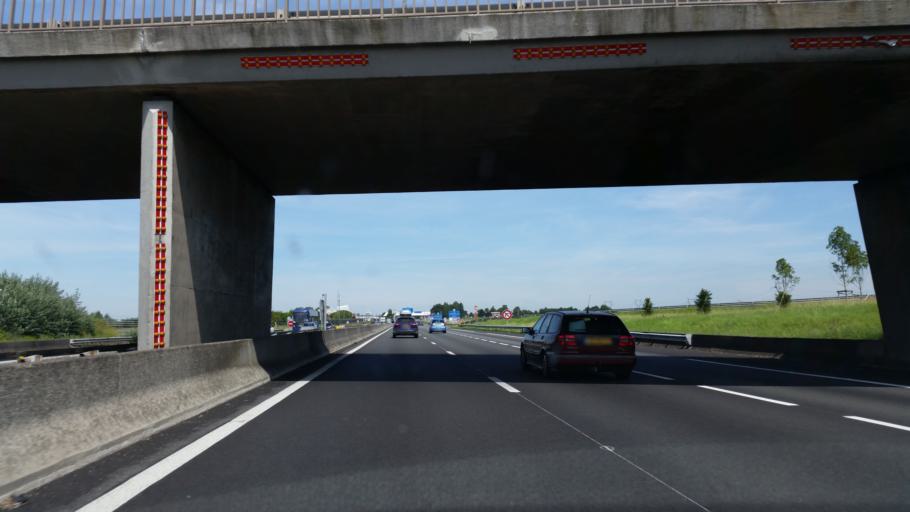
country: FR
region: Picardie
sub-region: Departement de la Somme
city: Chaulnes
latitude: 49.8785
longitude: 2.8370
